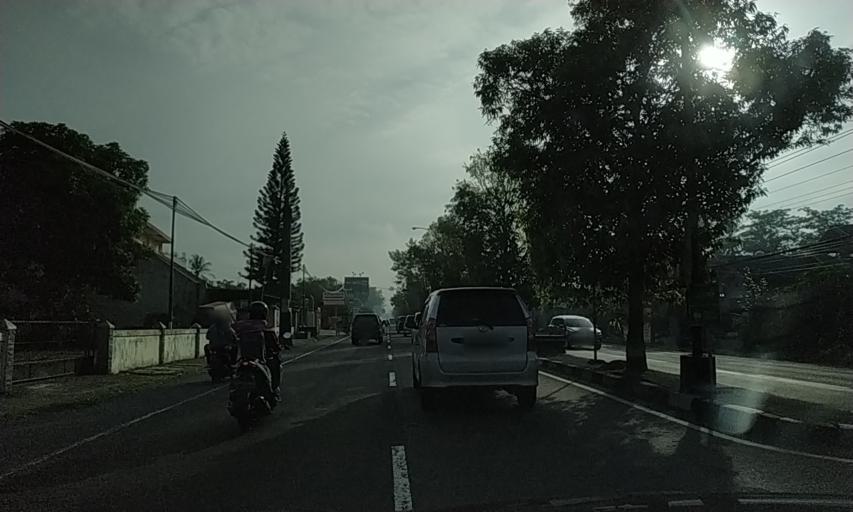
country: ID
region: Central Java
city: Candi Prambanan
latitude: -7.7659
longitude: 110.4725
